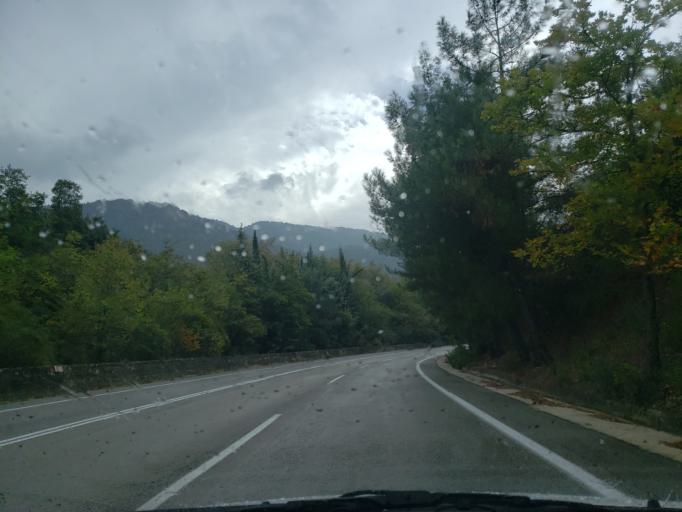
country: GR
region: Central Greece
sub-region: Nomos Fthiotidos
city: Anthili
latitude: 38.7884
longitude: 22.4942
